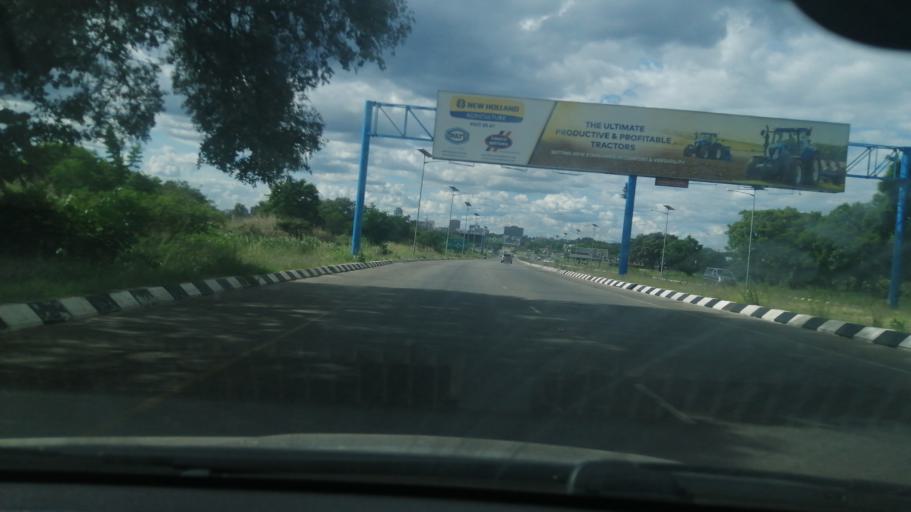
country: ZW
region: Harare
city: Harare
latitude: -17.8541
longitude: 31.0633
